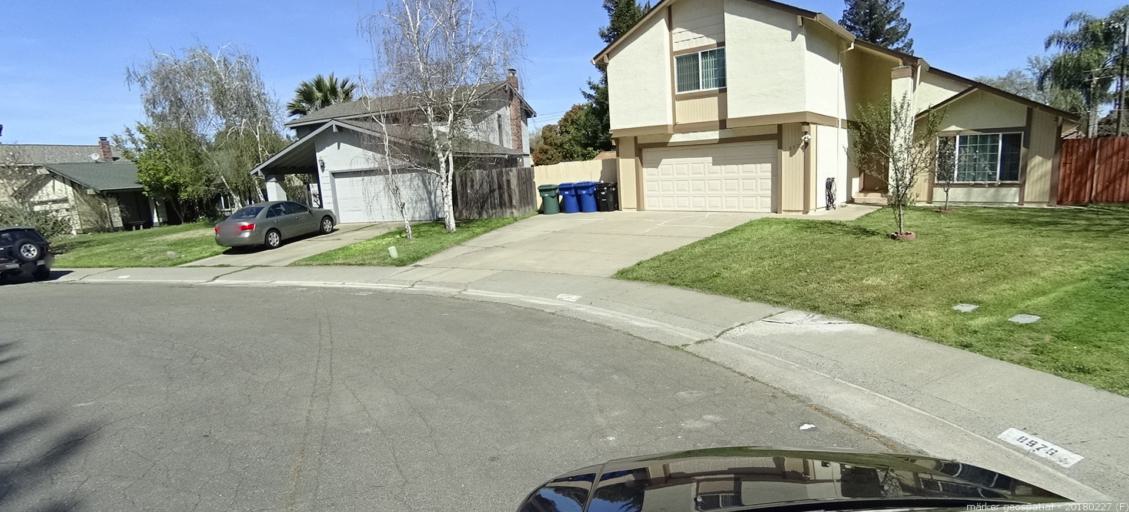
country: US
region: California
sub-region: Sacramento County
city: Rosemont
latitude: 38.5501
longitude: -121.3681
